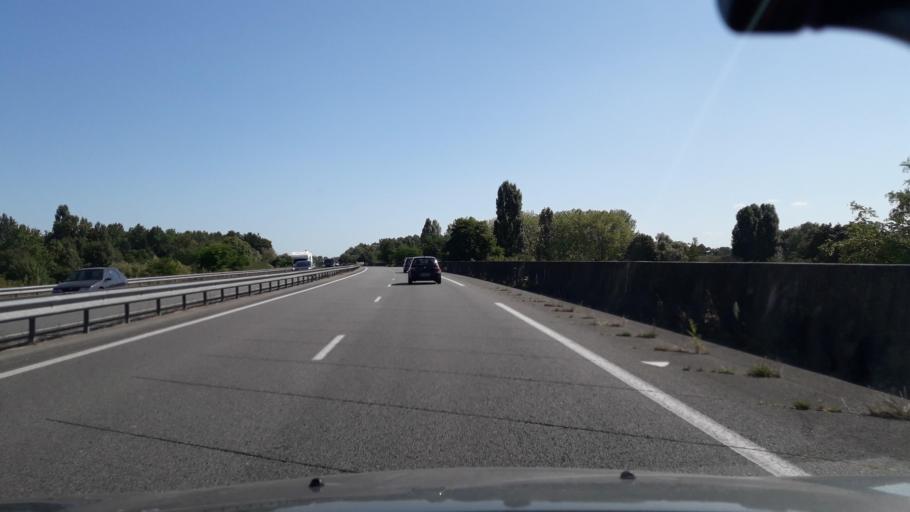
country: FR
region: Poitou-Charentes
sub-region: Departement de la Charente
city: Jarnac
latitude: 45.6664
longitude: -0.1730
